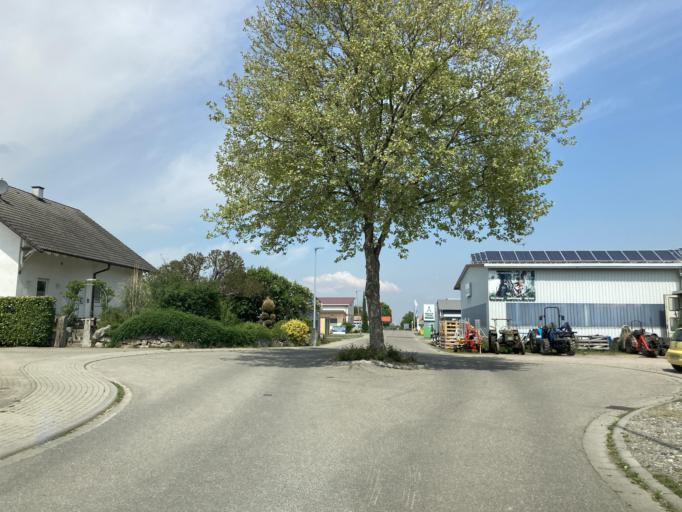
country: DE
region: Baden-Wuerttemberg
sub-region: Freiburg Region
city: Schliengen
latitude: 47.7621
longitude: 7.5772
